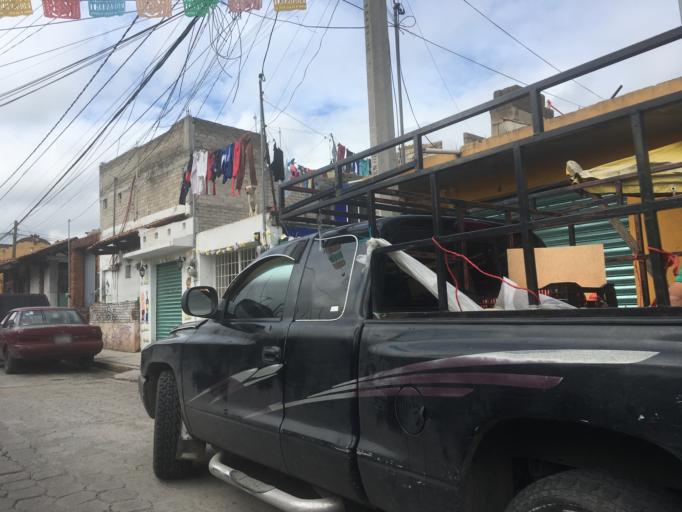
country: MX
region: Morelos
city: Metepec
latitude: 19.2605
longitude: -99.6079
